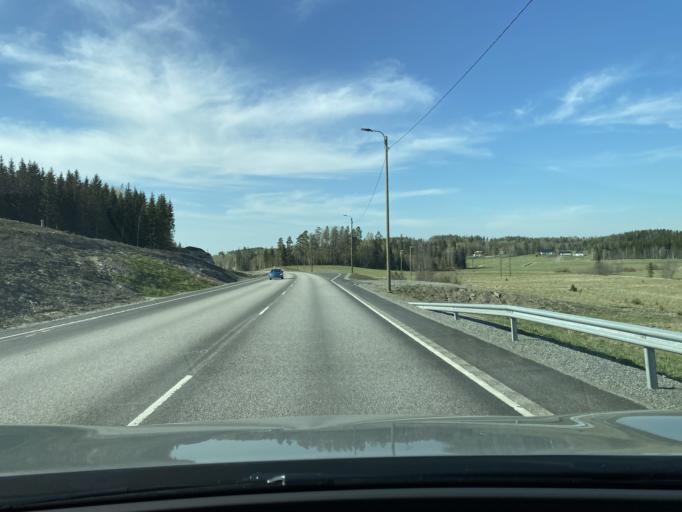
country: FI
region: Uusimaa
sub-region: Helsinki
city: Nurmijaervi
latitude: 60.4136
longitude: 24.7476
